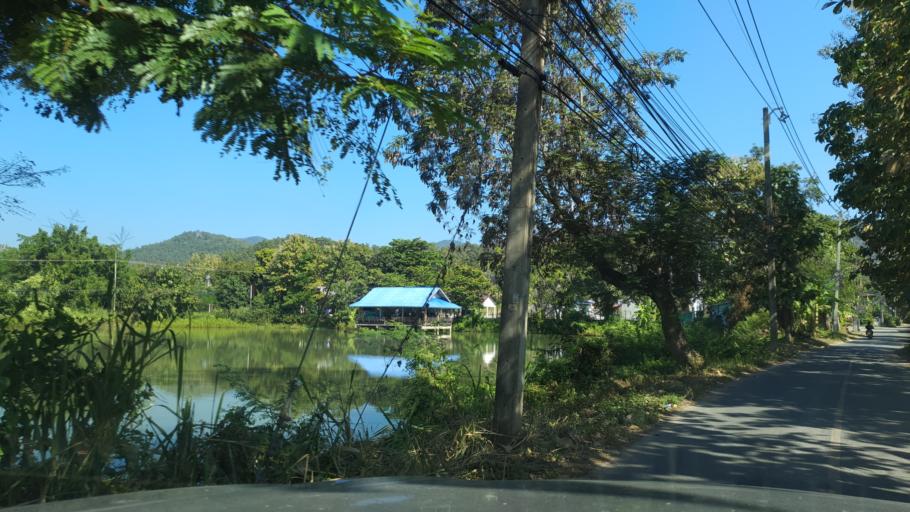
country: TH
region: Chiang Mai
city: San Sai
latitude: 18.8872
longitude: 99.1654
